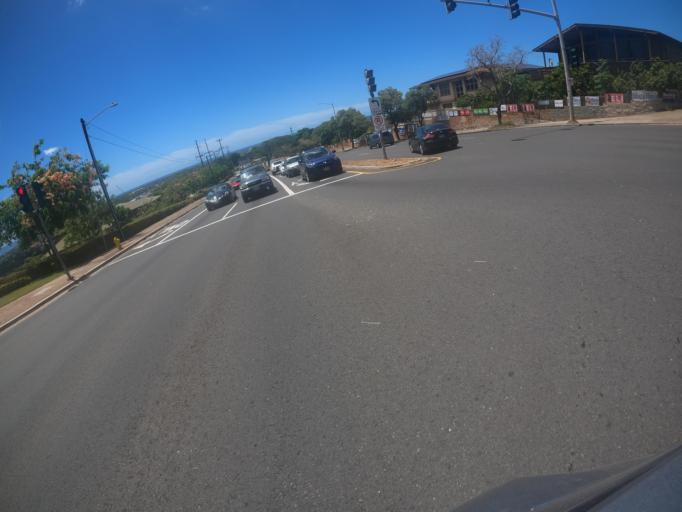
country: US
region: Hawaii
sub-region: Honolulu County
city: Makakilo City
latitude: 21.3444
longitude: -158.0797
